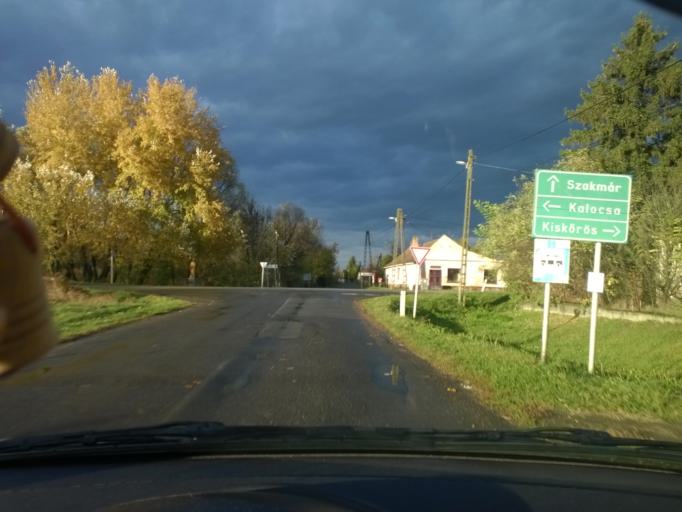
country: HU
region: Bacs-Kiskun
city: Kalocsa
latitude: 46.5090
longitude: 19.0532
